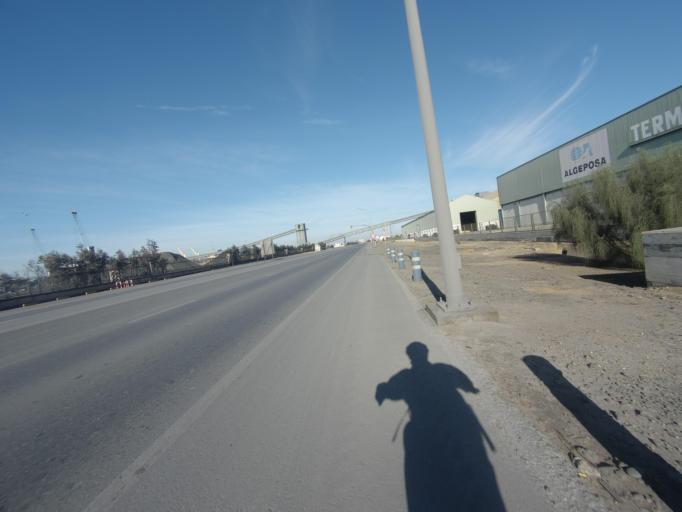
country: ES
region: Andalusia
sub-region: Provincia de Huelva
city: Punta Umbria
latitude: 37.1953
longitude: -6.9327
